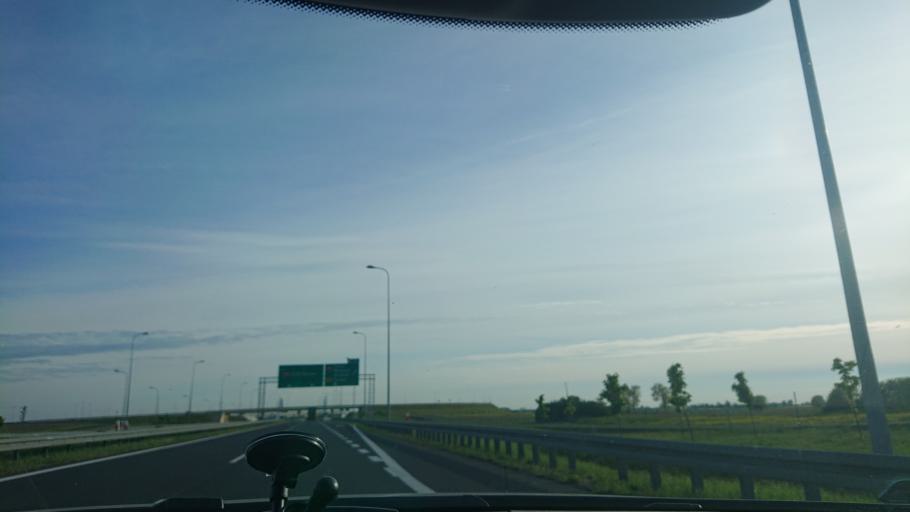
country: PL
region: Greater Poland Voivodeship
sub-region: Powiat gnieznienski
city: Lubowo
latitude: 52.5266
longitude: 17.5108
